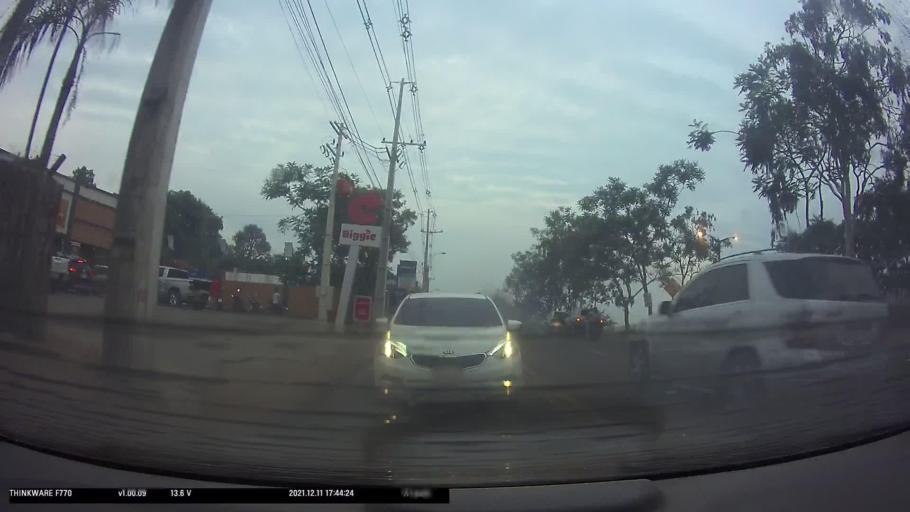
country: PY
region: Cordillera
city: San Bernardino
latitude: -25.2975
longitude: -57.2702
